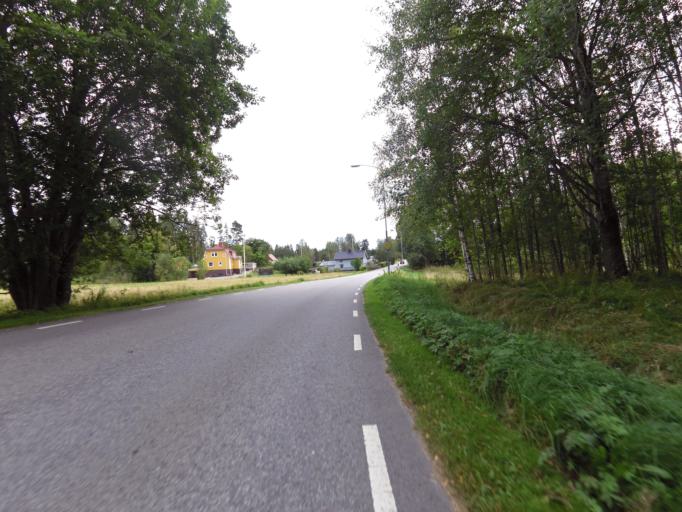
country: SE
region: Gaevleborg
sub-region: Gavle Kommun
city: Valbo
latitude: 60.6558
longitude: 16.9792
